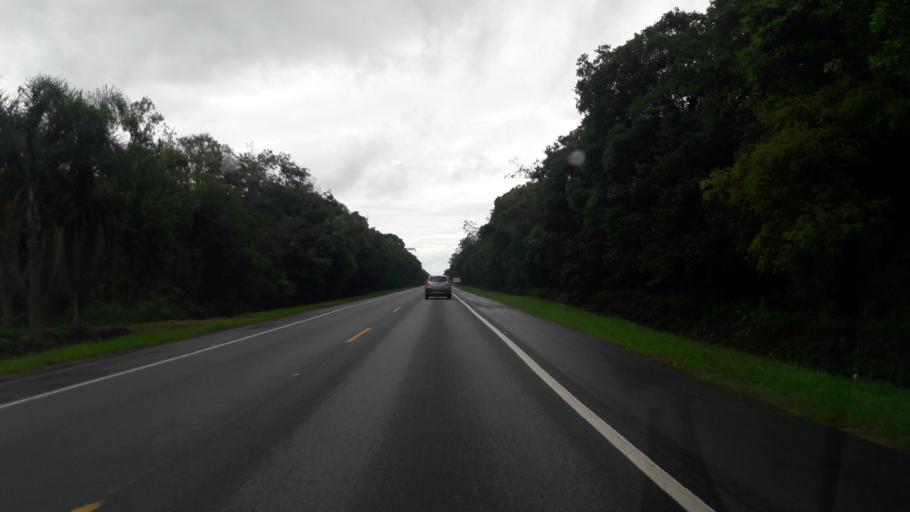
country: BR
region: Parana
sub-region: Pontal Do Parana
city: Pontal do Parana
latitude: -25.6364
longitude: -48.5355
